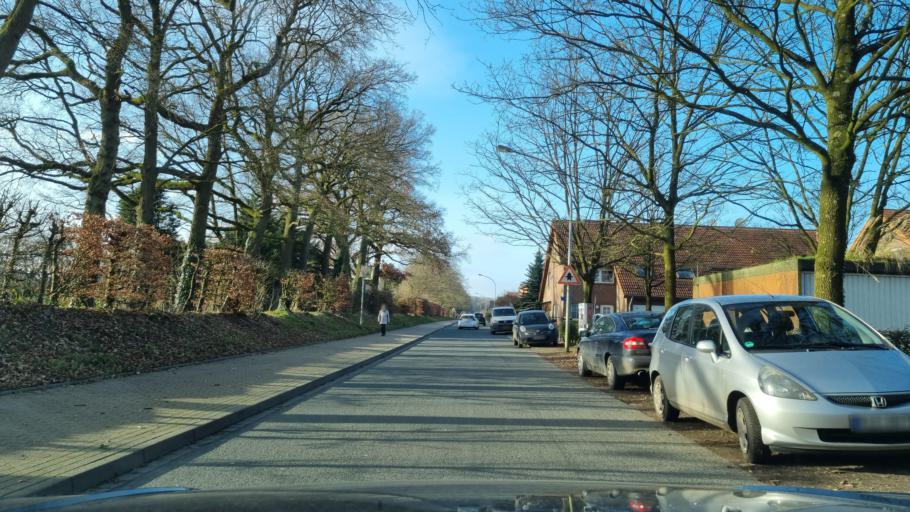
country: DE
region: North Rhine-Westphalia
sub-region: Regierungsbezirk Dusseldorf
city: Kleve
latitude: 51.7659
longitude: 6.1066
